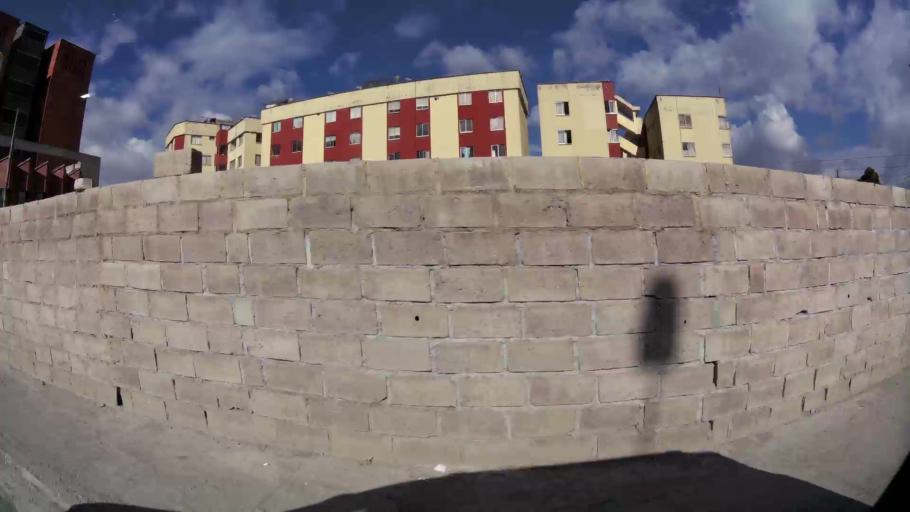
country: EC
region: Pichincha
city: Quito
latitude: -0.2122
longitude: -78.4884
